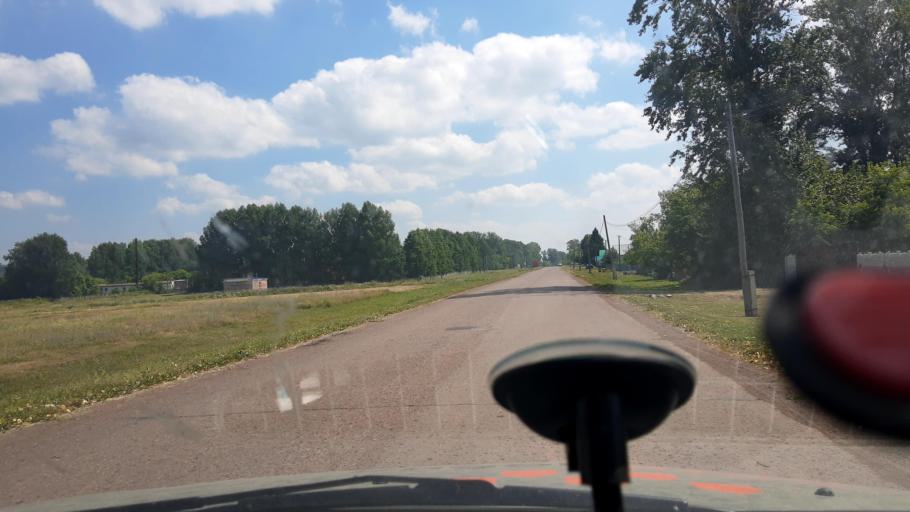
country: RU
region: Bashkortostan
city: Chekmagush
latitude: 54.8786
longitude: 54.6085
